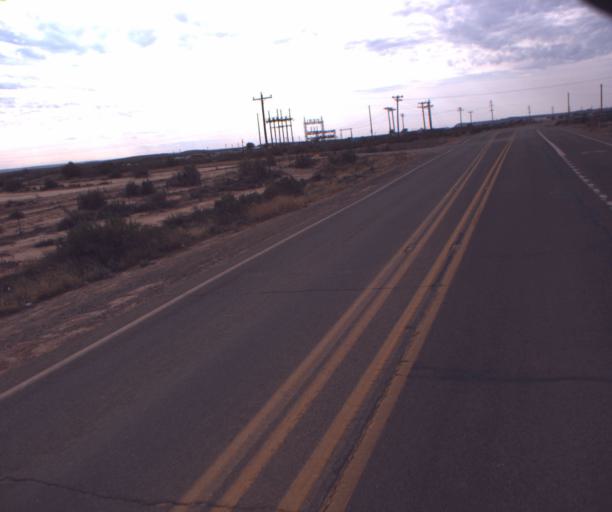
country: US
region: Arizona
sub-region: Apache County
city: Many Farms
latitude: 36.3654
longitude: -109.6139
